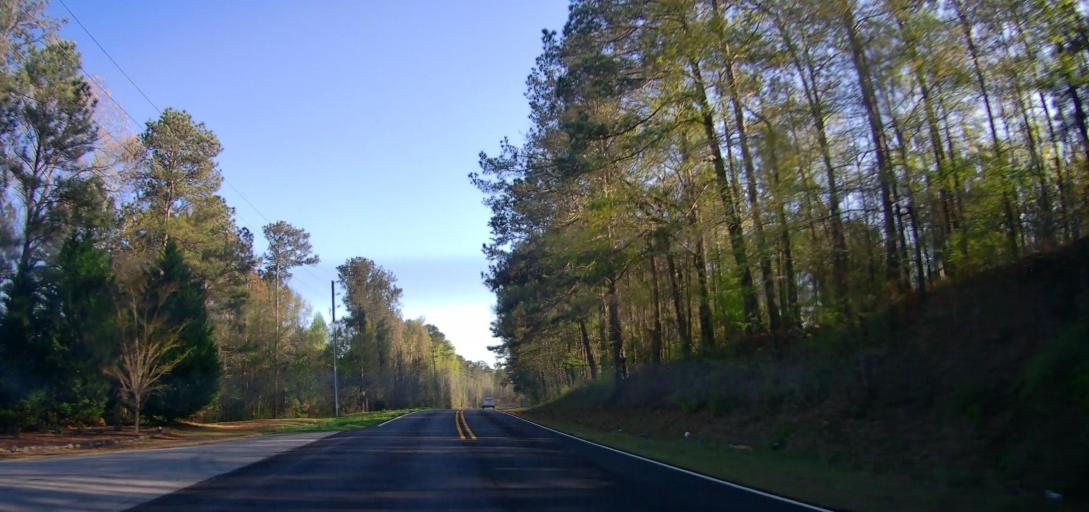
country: US
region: Georgia
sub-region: Butts County
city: Jackson
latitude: 33.3630
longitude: -83.9096
